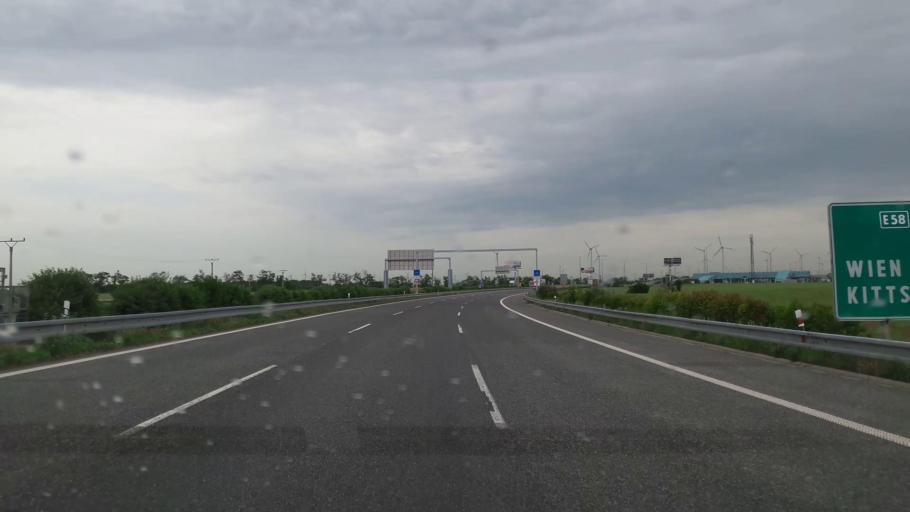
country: AT
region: Burgenland
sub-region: Politischer Bezirk Neusiedl am See
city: Kittsee
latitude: 48.0705
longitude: 17.0854
